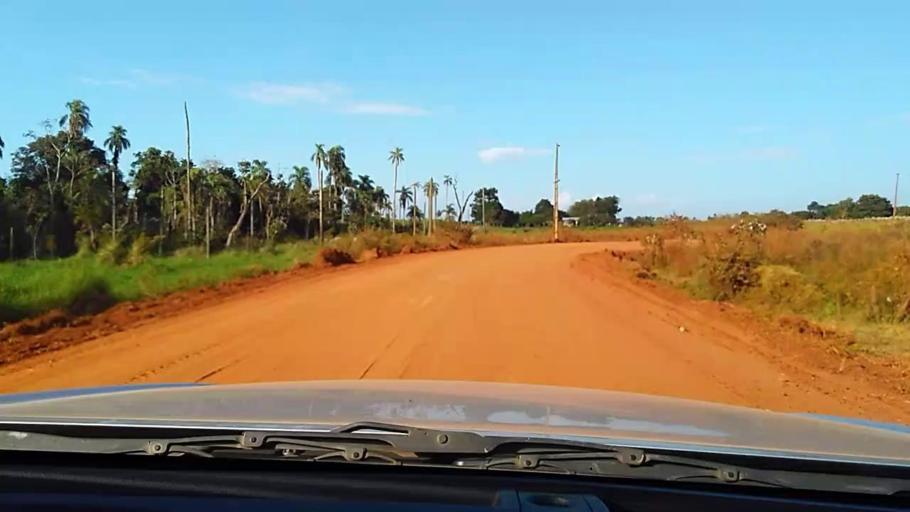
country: PY
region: Alto Parana
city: Santa Rita
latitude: -25.7056
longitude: -55.3825
